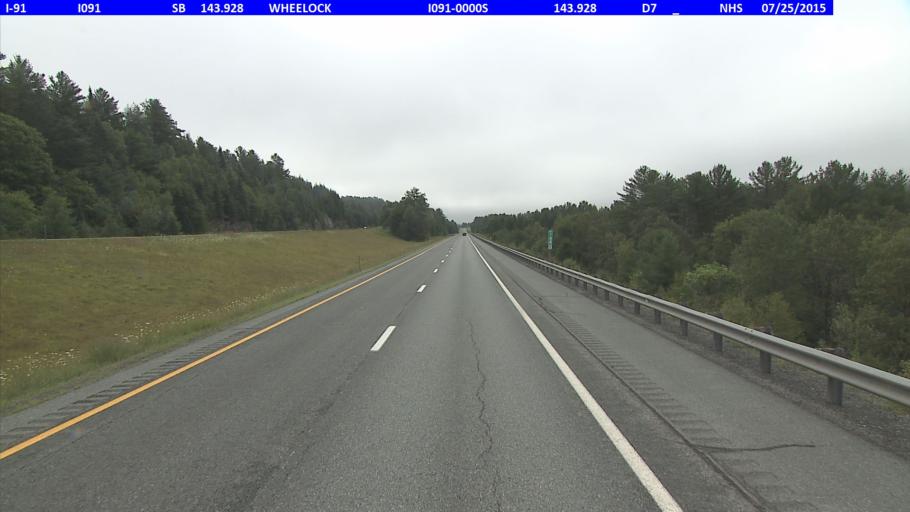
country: US
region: Vermont
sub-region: Caledonia County
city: Lyndonville
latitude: 44.5905
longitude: -72.0849
